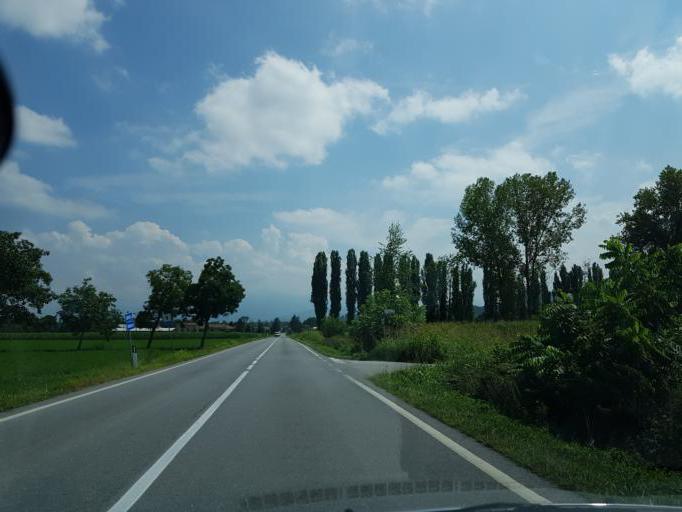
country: IT
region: Piedmont
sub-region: Provincia di Cuneo
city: Bernezzo
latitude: 44.3984
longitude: 7.4510
